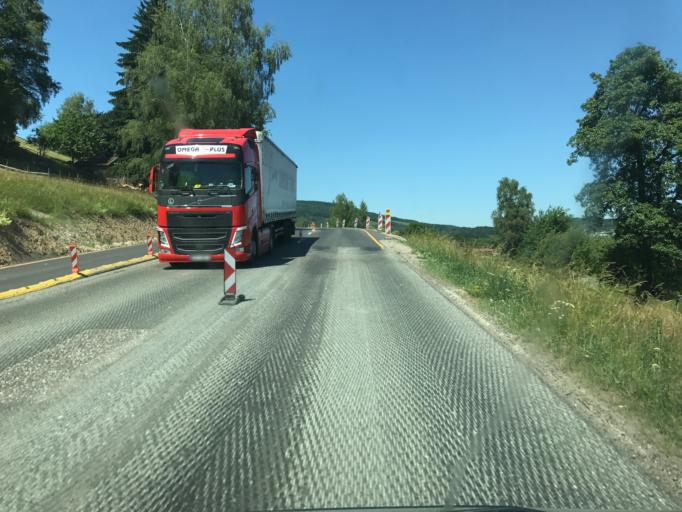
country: DE
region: Bavaria
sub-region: Upper Palatinate
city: Furth im Wald
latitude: 49.3299
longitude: 12.8468
